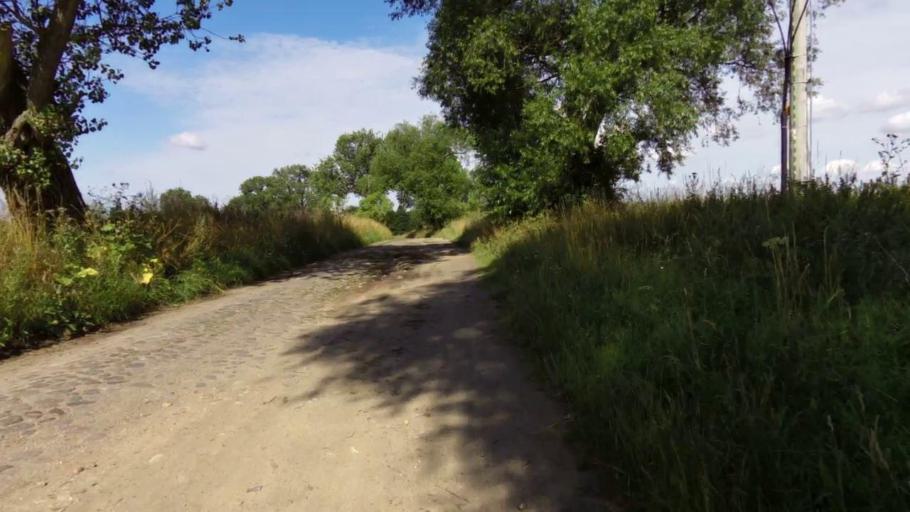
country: PL
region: West Pomeranian Voivodeship
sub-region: Powiat stargardzki
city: Stara Dabrowa
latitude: 53.3505
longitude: 15.1299
